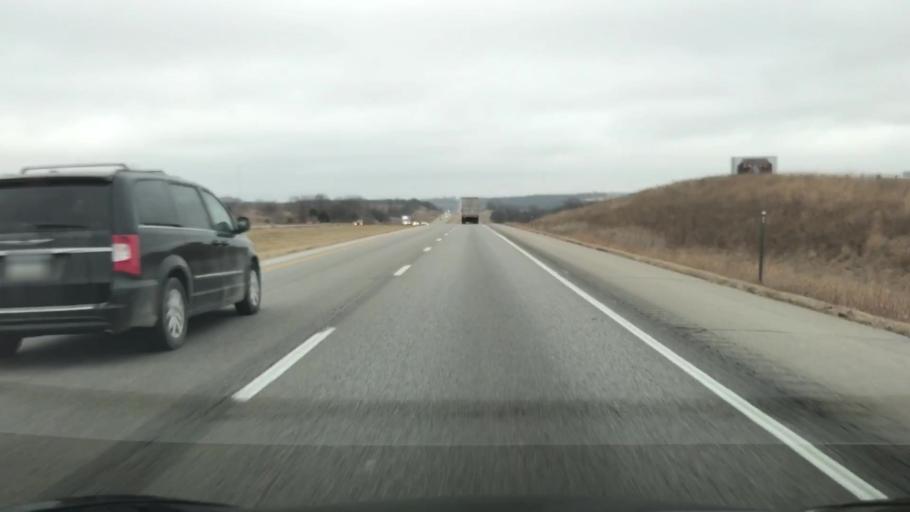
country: US
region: Iowa
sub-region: Madison County
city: Earlham
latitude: 41.5178
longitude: -94.1715
